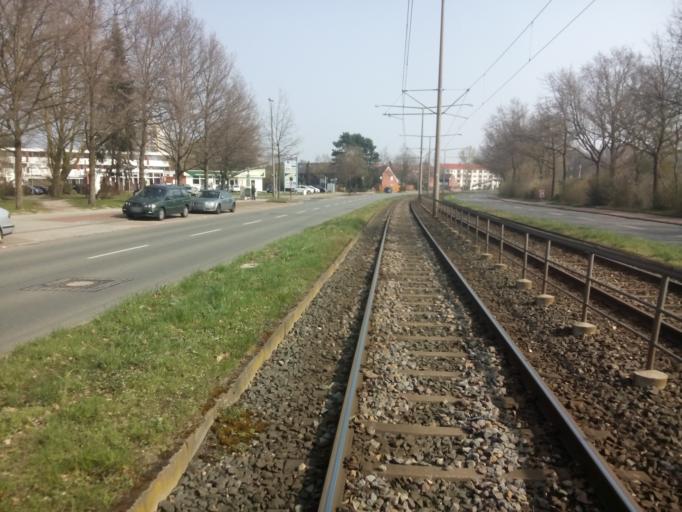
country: DE
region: Bremen
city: Bremen
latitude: 53.0767
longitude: 8.8715
